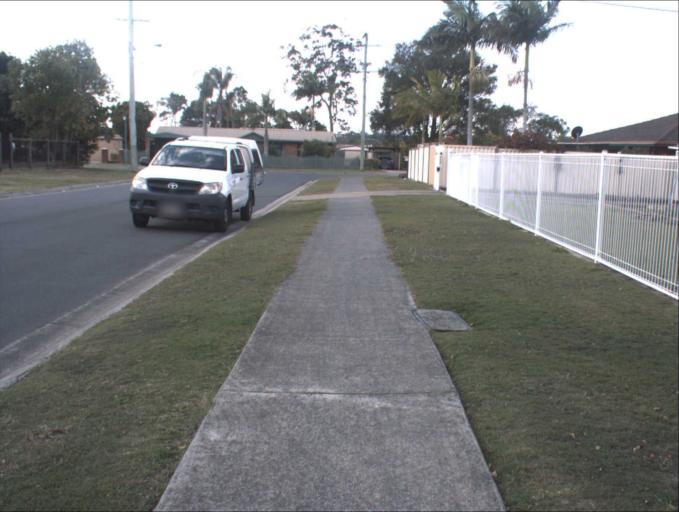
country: AU
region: Queensland
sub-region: Brisbane
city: Sunnybank Hills
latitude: -27.6668
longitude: 153.0443
